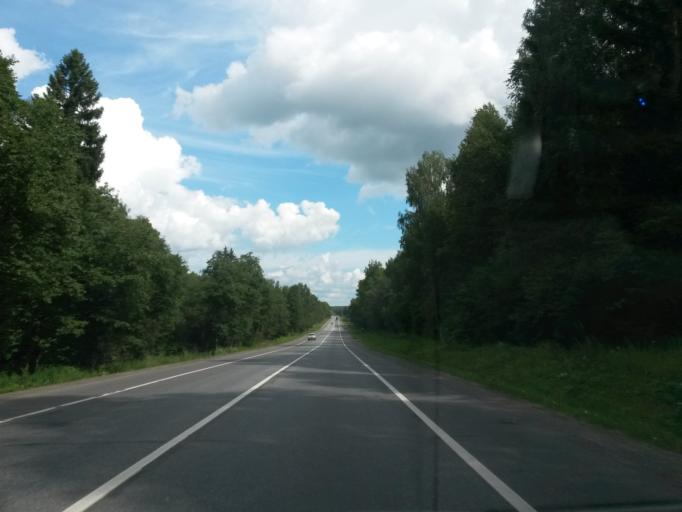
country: RU
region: Jaroslavl
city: Pereslavl'-Zalesskiy
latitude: 56.6784
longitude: 38.7334
